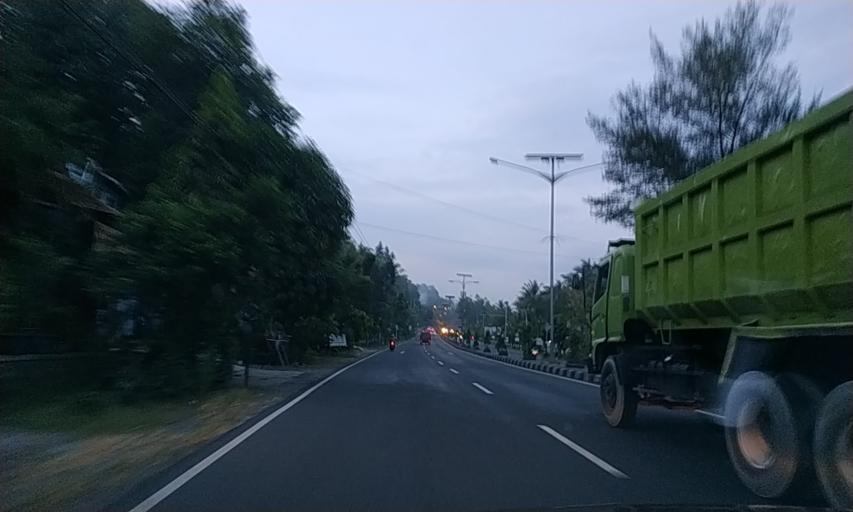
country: ID
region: Daerah Istimewa Yogyakarta
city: Srandakan
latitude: -7.8546
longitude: 110.2157
